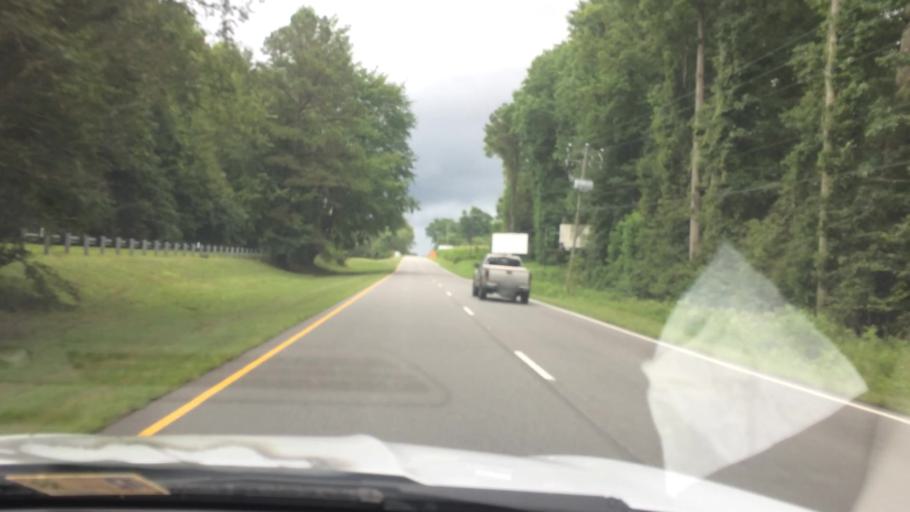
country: US
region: Virginia
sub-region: King William County
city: West Point
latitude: 37.4030
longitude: -76.8227
